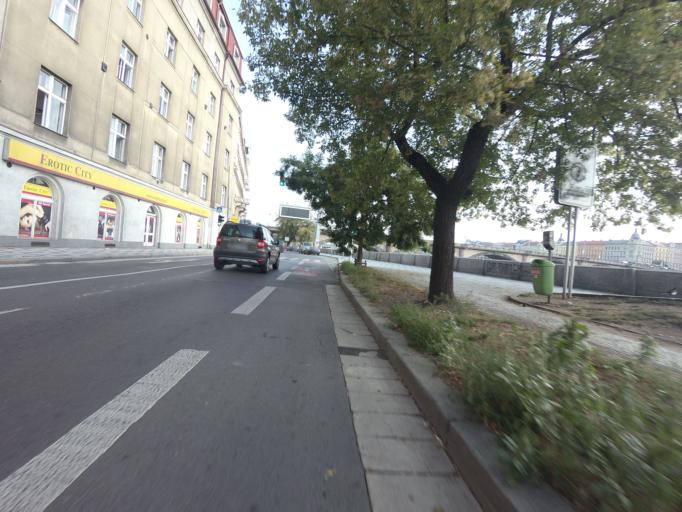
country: CZ
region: Praha
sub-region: Praha 2
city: Vysehrad
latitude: 50.0714
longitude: 14.4102
